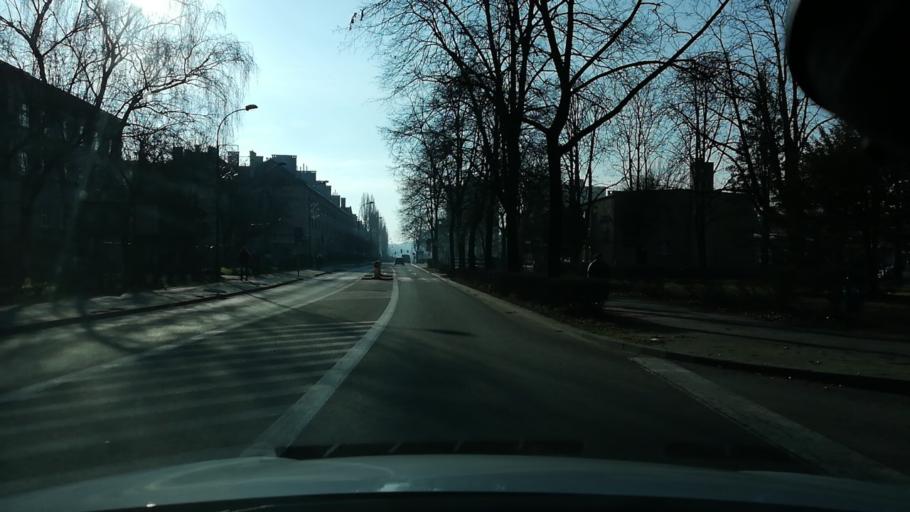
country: PL
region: Silesian Voivodeship
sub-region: Swietochlowice
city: Swietochlowice
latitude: 50.2695
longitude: 18.9376
